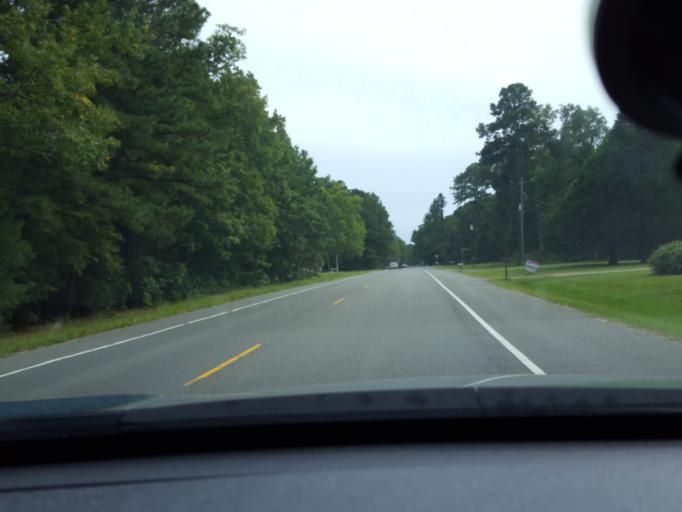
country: US
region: Virginia
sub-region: Hanover County
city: Hanover
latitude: 37.7768
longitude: -77.3709
